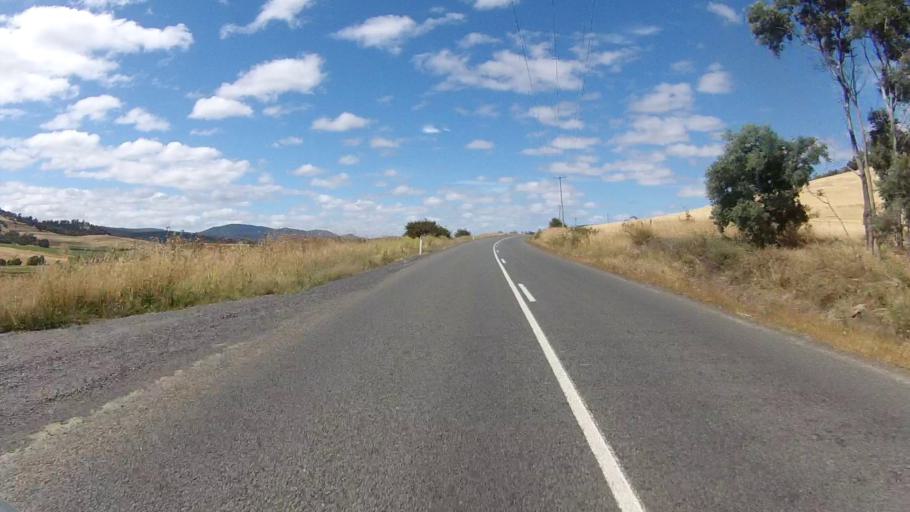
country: AU
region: Tasmania
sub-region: Brighton
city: Old Beach
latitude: -42.5979
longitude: 147.4151
